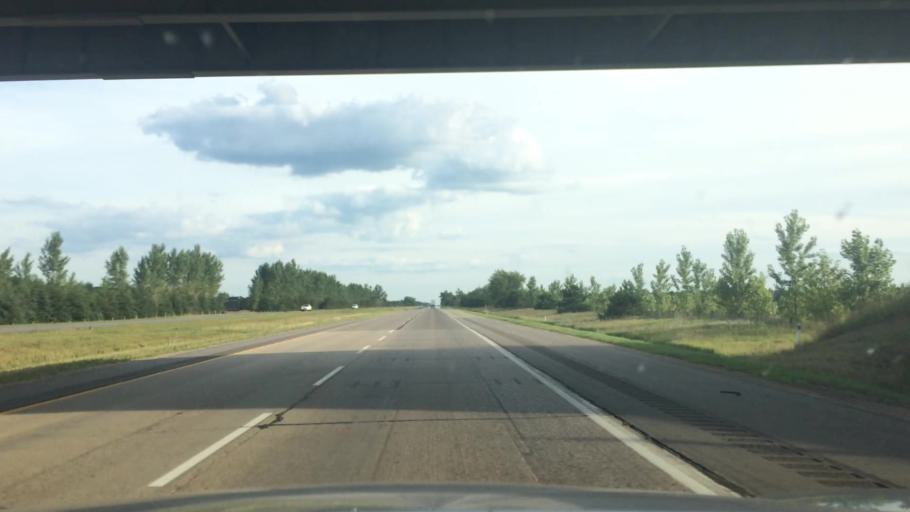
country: US
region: Wisconsin
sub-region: Portage County
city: Plover
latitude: 44.2879
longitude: -89.5237
